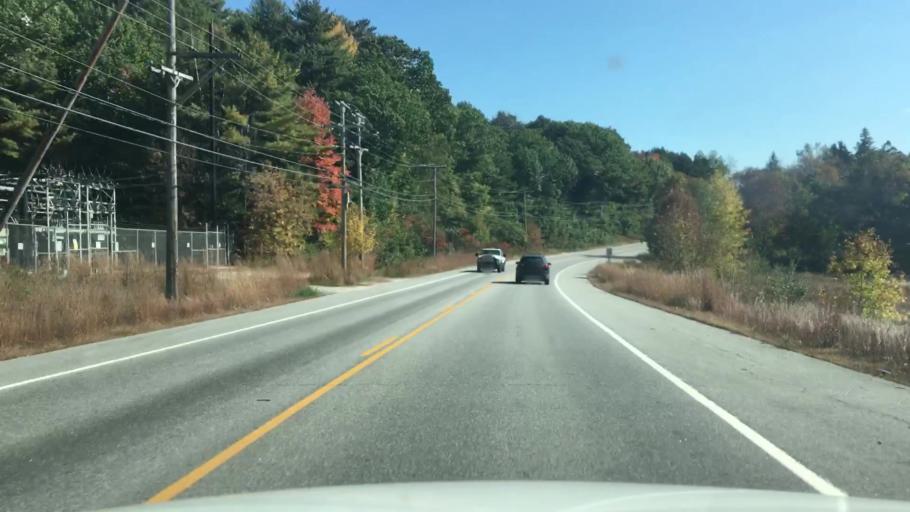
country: US
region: Maine
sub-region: Androscoggin County
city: Lisbon Falls
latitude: 43.9920
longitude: -70.0489
